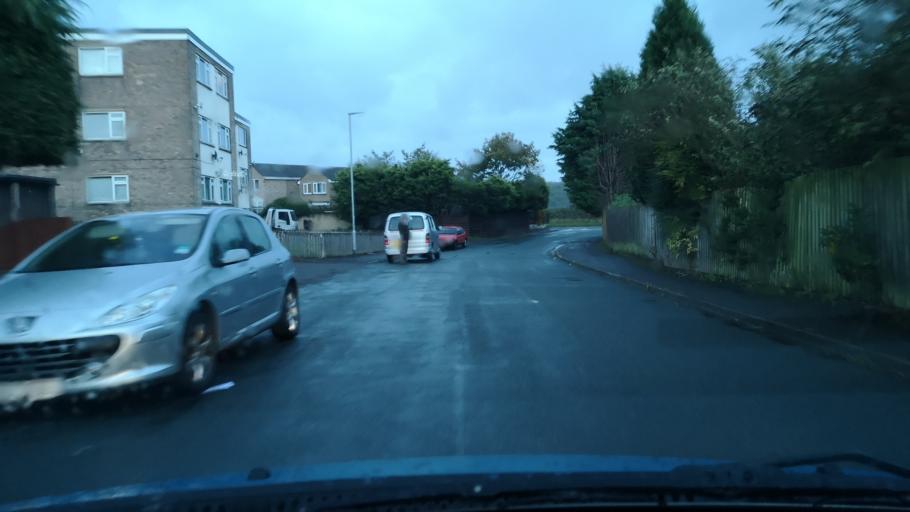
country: GB
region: England
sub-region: City and Borough of Leeds
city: Gildersome
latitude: 53.7343
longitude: -1.6423
